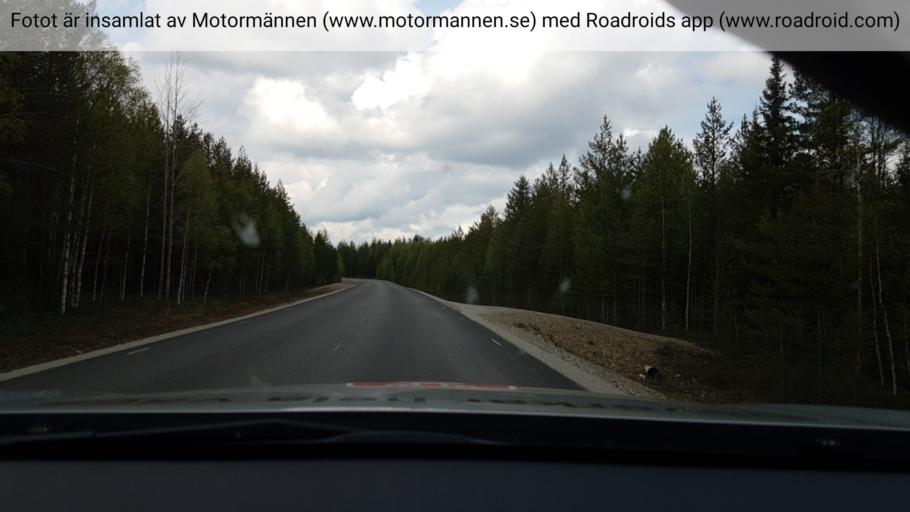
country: SE
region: Vaesterbotten
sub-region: Lycksele Kommun
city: Lycksele
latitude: 64.0418
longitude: 18.4427
